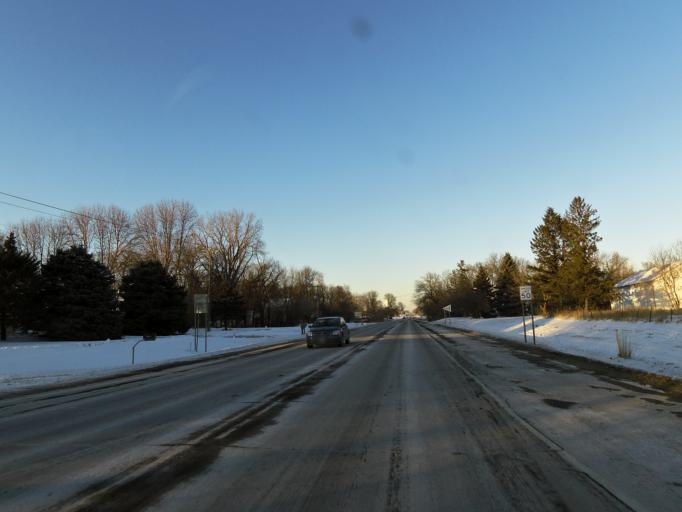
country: US
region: Minnesota
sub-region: Dakota County
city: Farmington
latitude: 44.6525
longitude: -93.1367
